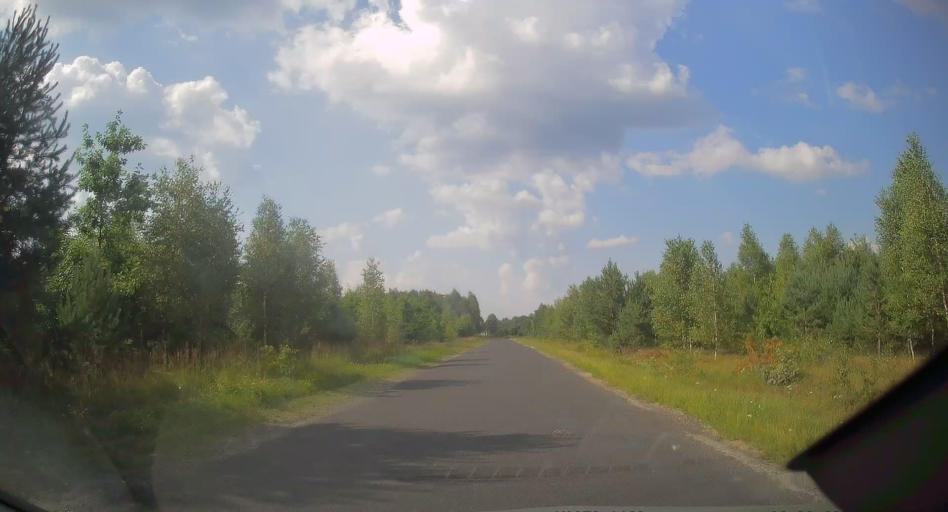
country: PL
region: Swietokrzyskie
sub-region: Powiat konecki
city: Radoszyce
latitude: 51.1078
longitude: 20.2646
